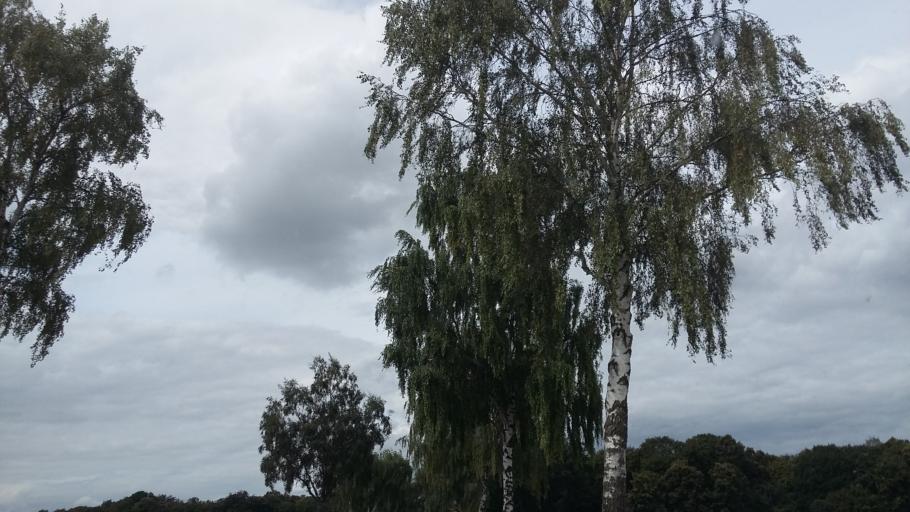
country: DE
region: Lower Saxony
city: Harsum
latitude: 52.2131
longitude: 9.9498
